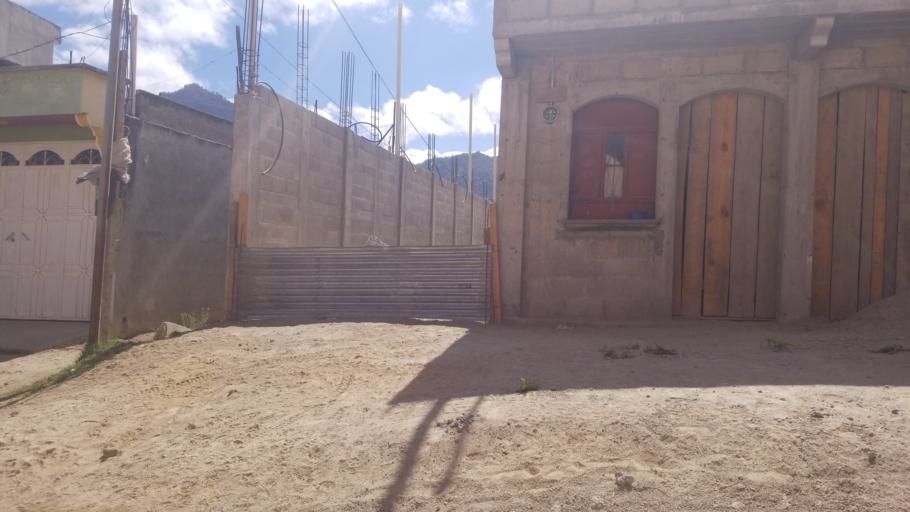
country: GT
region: Quetzaltenango
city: Quetzaltenango
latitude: 14.7888
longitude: -91.5481
